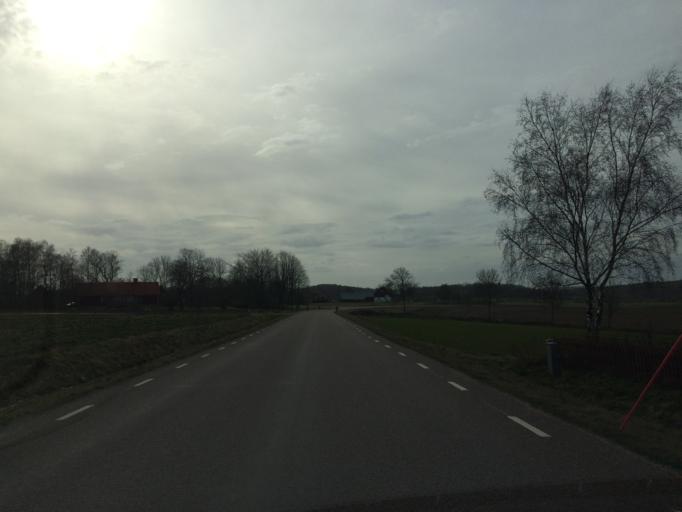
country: SE
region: Halland
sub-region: Halmstads Kommun
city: Getinge
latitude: 56.8583
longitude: 12.6404
